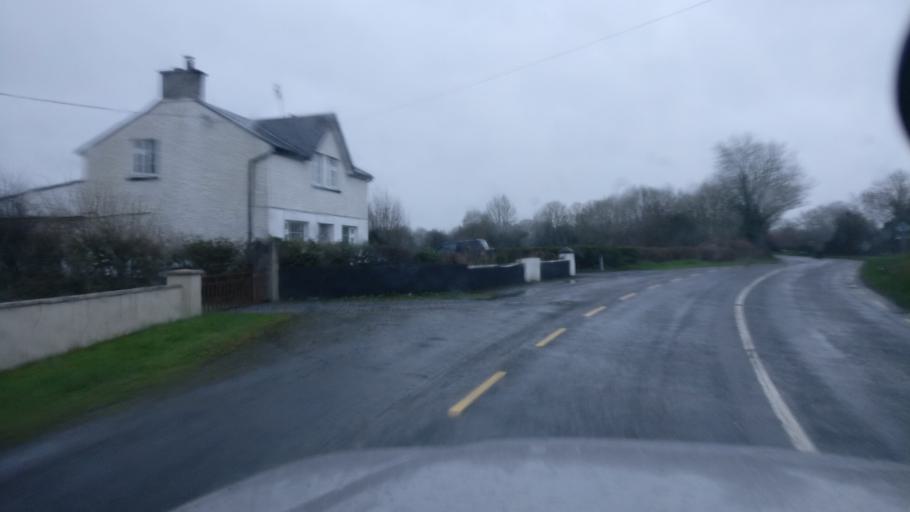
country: IE
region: Connaught
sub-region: County Galway
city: Portumna
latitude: 53.1402
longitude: -8.1960
